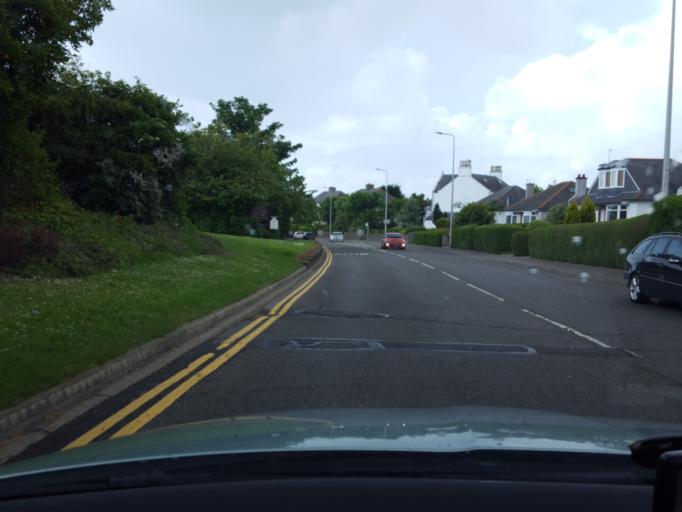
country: GB
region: Scotland
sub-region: Angus
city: Arbroath
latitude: 56.5680
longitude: -2.5796
